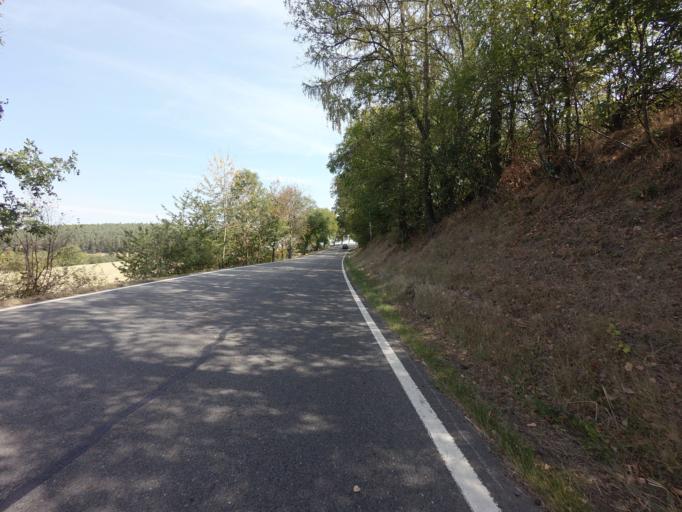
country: CZ
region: Central Bohemia
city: Petrovice
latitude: 49.5774
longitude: 14.3763
